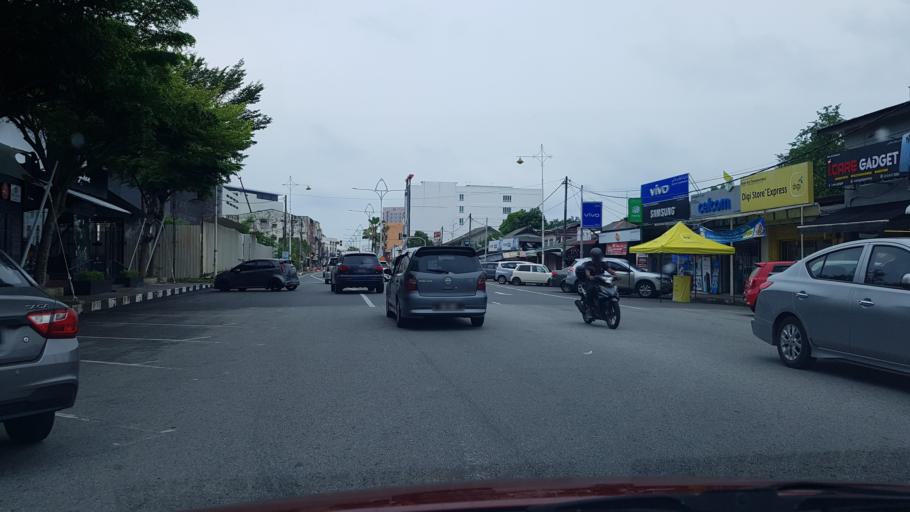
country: MY
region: Terengganu
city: Kuala Terengganu
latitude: 5.3368
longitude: 103.1412
